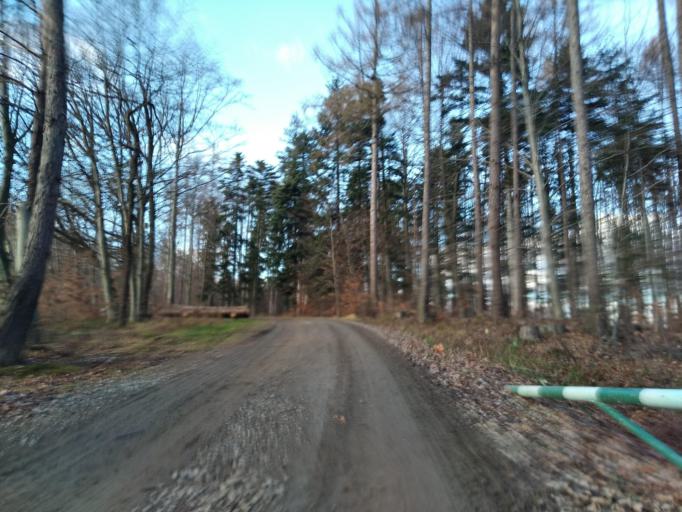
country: PL
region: Subcarpathian Voivodeship
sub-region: Powiat strzyzowski
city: Babica
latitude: 49.9501
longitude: 21.8719
